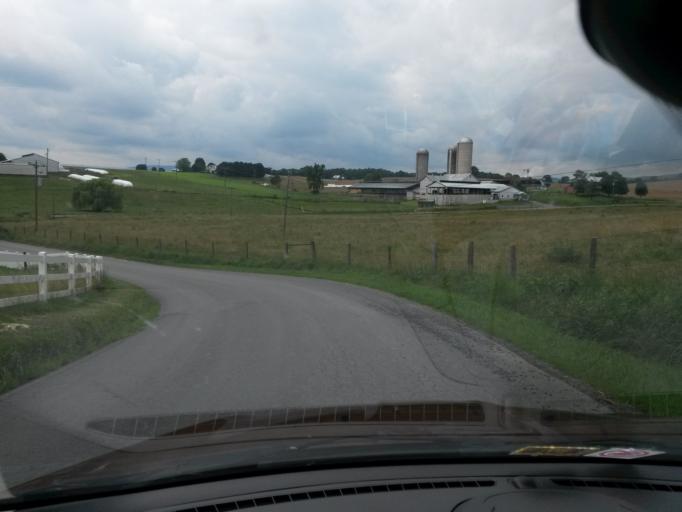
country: US
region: Virginia
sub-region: Rockingham County
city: Dayton
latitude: 38.4472
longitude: -78.9662
